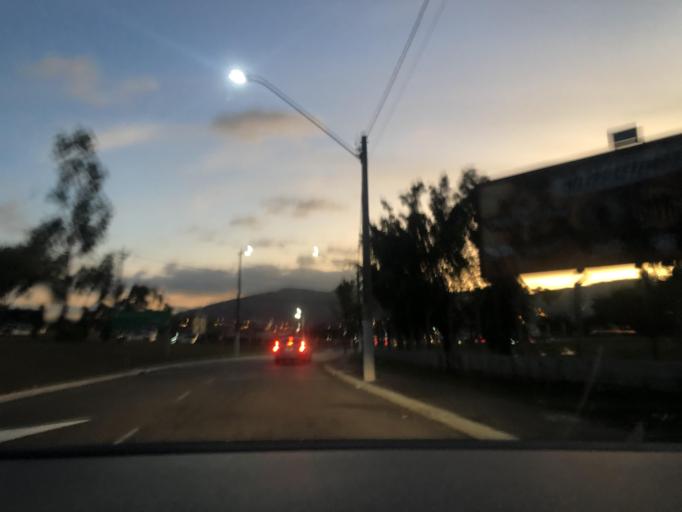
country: BR
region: Sao Paulo
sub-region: Jundiai
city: Jundiai
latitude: -23.2177
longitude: -46.8700
